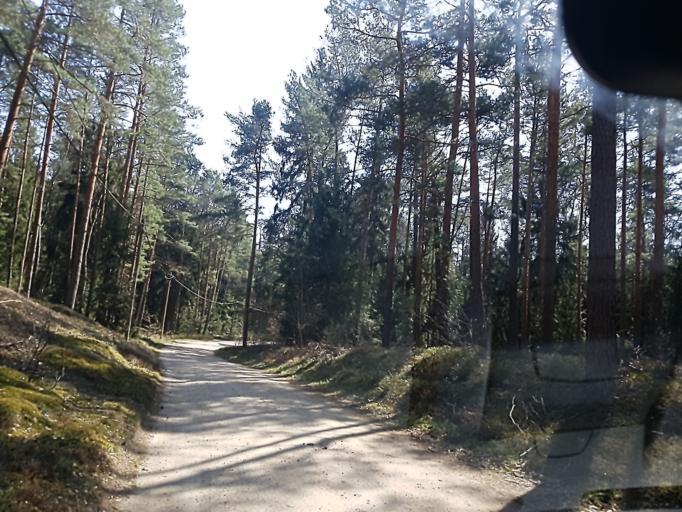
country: DE
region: Brandenburg
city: Schonborn
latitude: 51.5788
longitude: 13.4824
